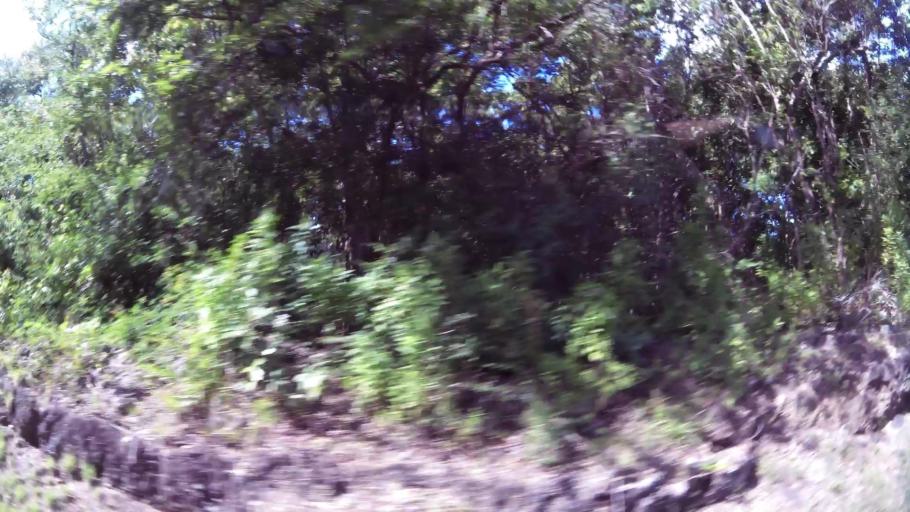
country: DM
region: Saint John
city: Portsmouth
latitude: 15.5906
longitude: -61.4638
